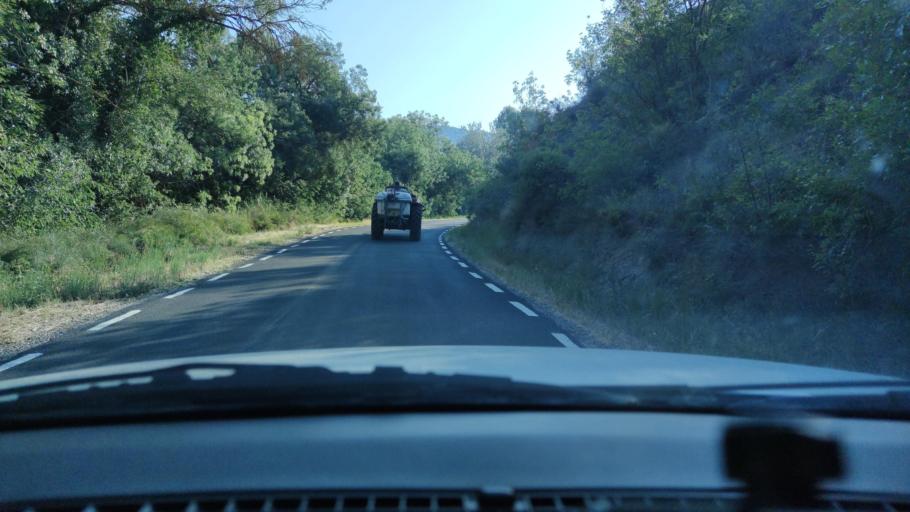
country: ES
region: Catalonia
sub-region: Provincia de Lleida
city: Camarasa
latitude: 41.8684
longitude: 0.8665
